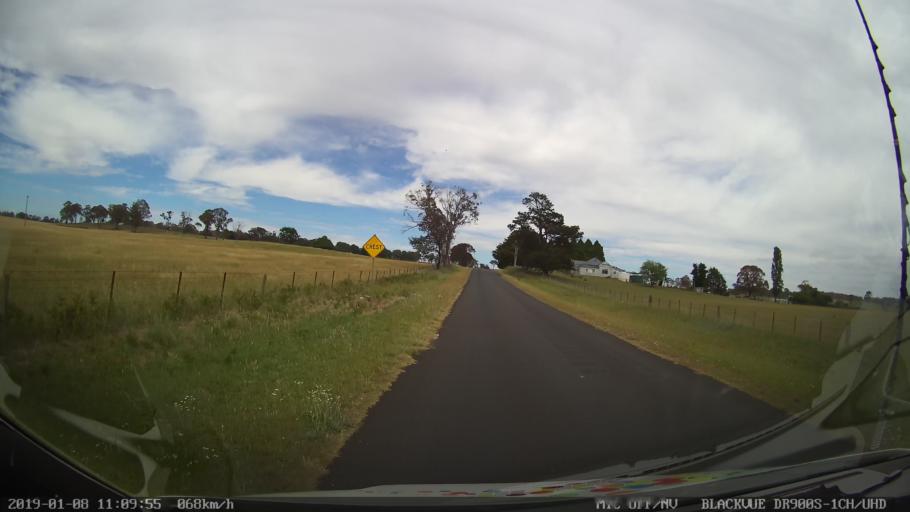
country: AU
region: New South Wales
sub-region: Guyra
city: Guyra
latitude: -30.2263
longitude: 151.6416
